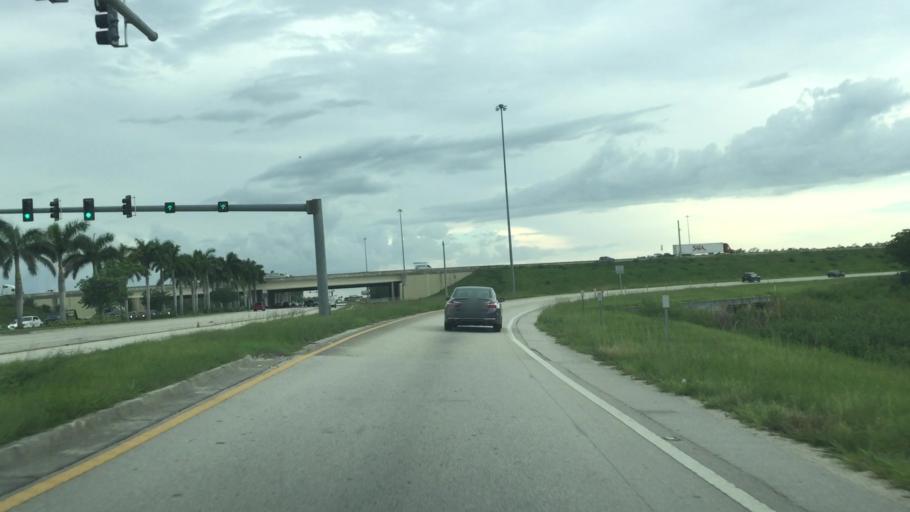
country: US
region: Florida
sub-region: Lee County
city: Three Oaks
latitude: 26.4933
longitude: -81.7916
